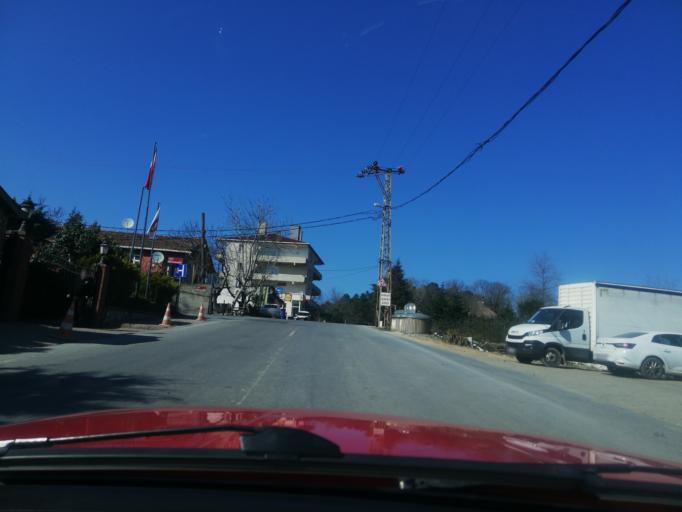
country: TR
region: Istanbul
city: Mahmut Sevket Pasa
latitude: 41.1073
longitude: 29.1605
